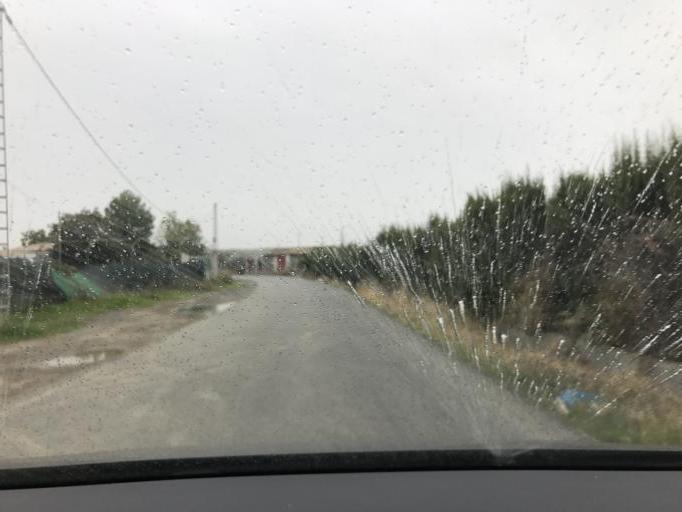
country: ES
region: Andalusia
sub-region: Provincia de Granada
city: Chauchina
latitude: 37.1834
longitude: -3.7253
